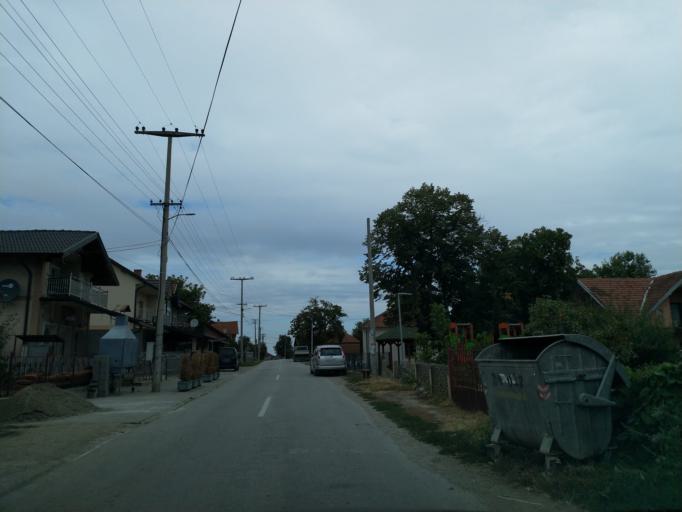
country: RS
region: Central Serbia
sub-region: Pomoravski Okrug
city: Cuprija
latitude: 43.8696
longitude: 21.3220
